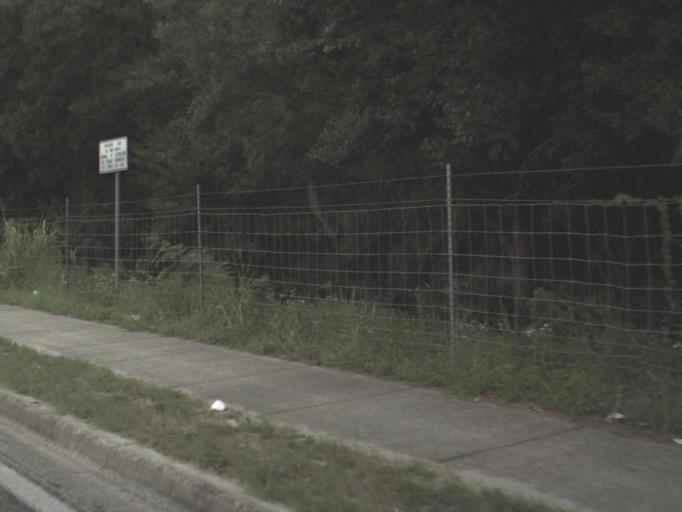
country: US
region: Florida
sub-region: Polk County
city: Eagle Lake
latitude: 27.9907
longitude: -81.7430
